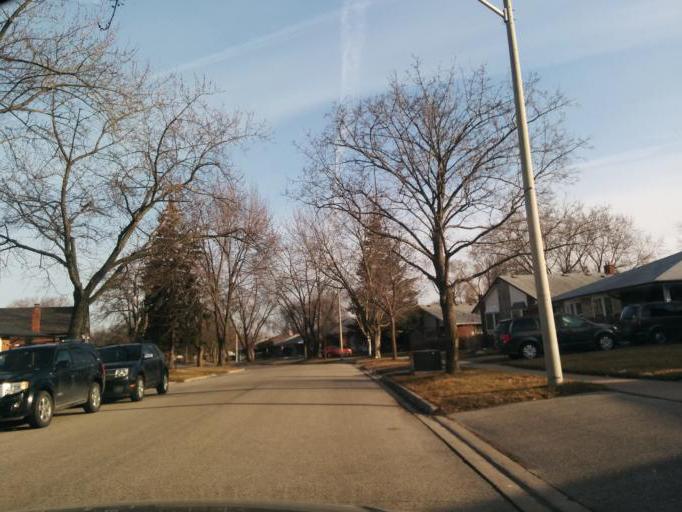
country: CA
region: Ontario
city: Etobicoke
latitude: 43.6096
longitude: -79.5991
